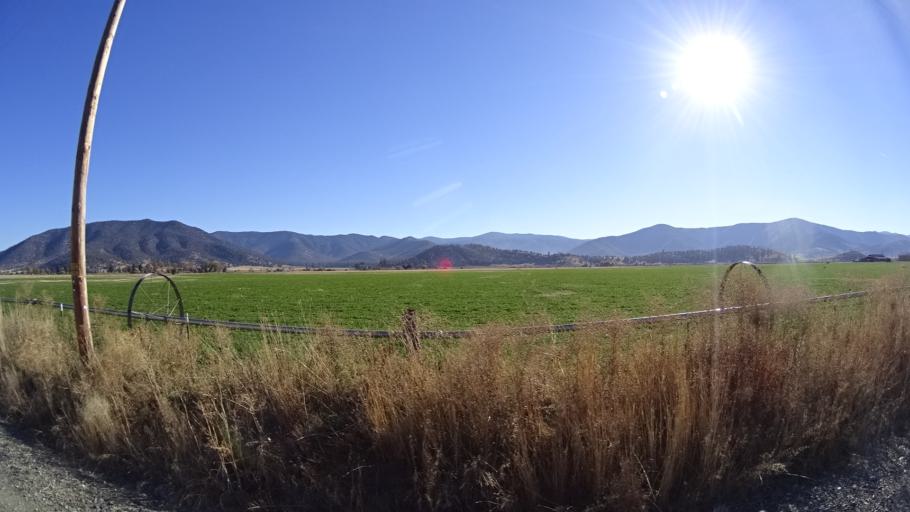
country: US
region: California
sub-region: Siskiyou County
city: Yreka
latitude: 41.4955
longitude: -122.8592
